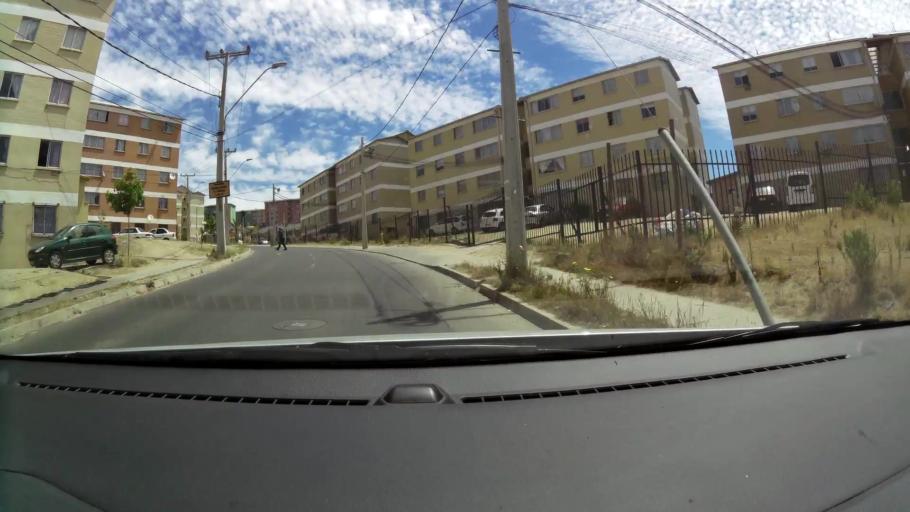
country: CL
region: Valparaiso
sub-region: Provincia de Valparaiso
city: Vina del Mar
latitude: -33.0625
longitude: -71.5638
